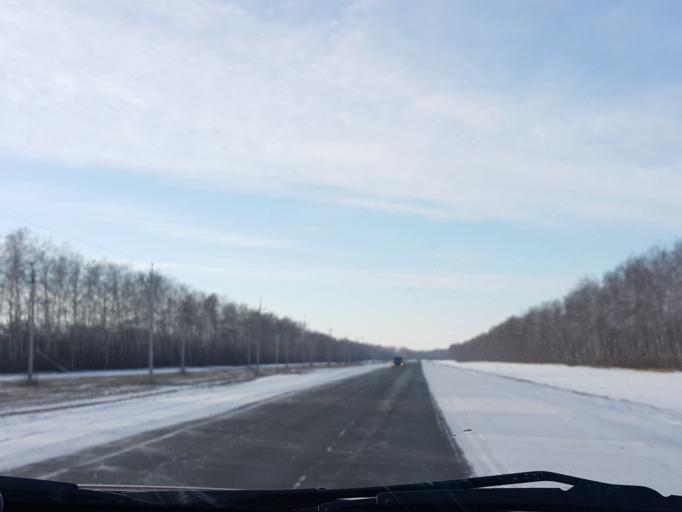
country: RU
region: Tambov
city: Znamenka
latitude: 52.3884
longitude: 41.3453
